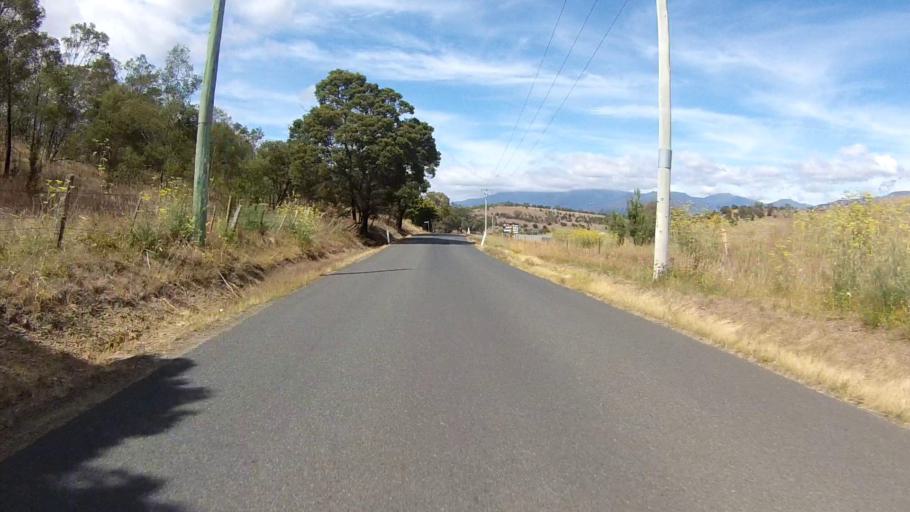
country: AU
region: Tasmania
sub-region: Brighton
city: Old Beach
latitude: -42.7451
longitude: 147.3016
